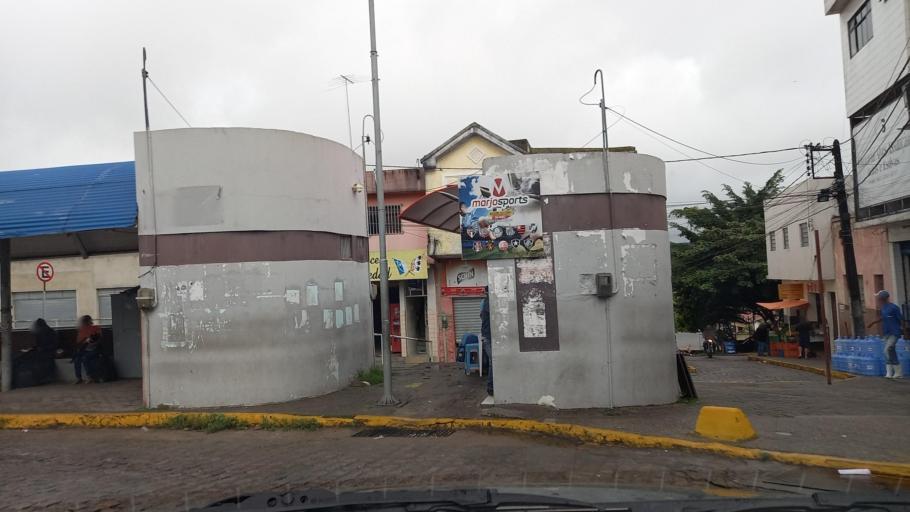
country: BR
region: Pernambuco
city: Garanhuns
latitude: -8.8908
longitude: -36.4970
